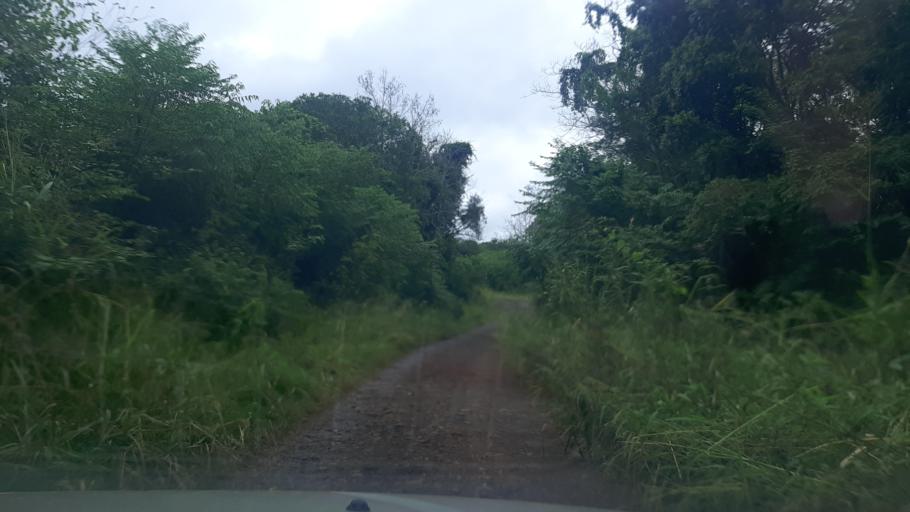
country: BR
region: Parana
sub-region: Ampere
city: Ampere
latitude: -26.0476
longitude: -53.5191
